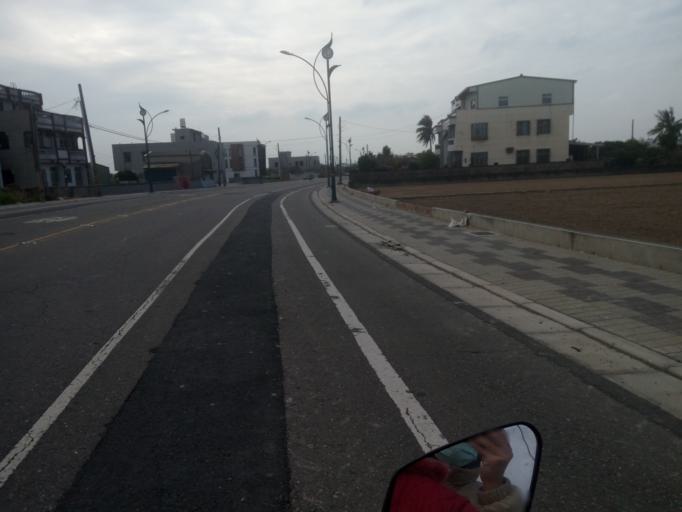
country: TW
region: Taiwan
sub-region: Chiayi
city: Taibao
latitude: 23.4908
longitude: 120.3522
